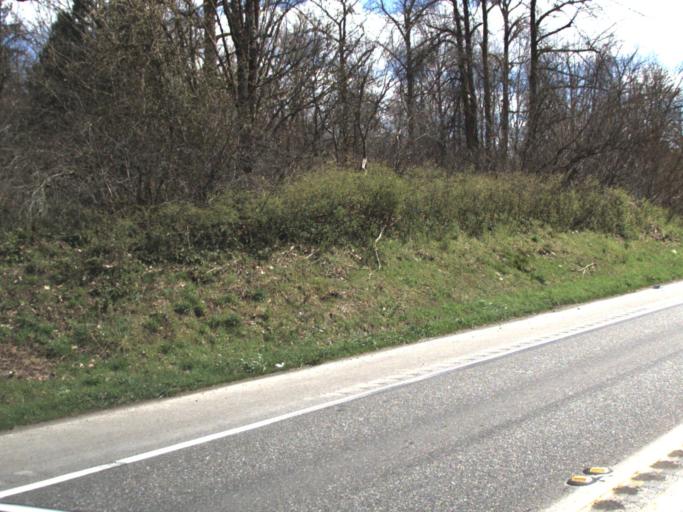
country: US
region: Washington
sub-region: King County
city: Maple Valley
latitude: 47.4258
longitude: -122.0526
